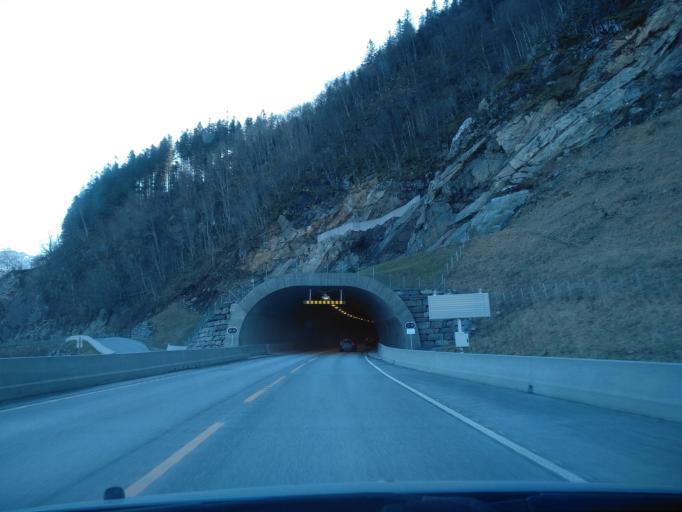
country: NO
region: Hordaland
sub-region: Etne
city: Etne
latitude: 59.7225
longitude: 6.1164
